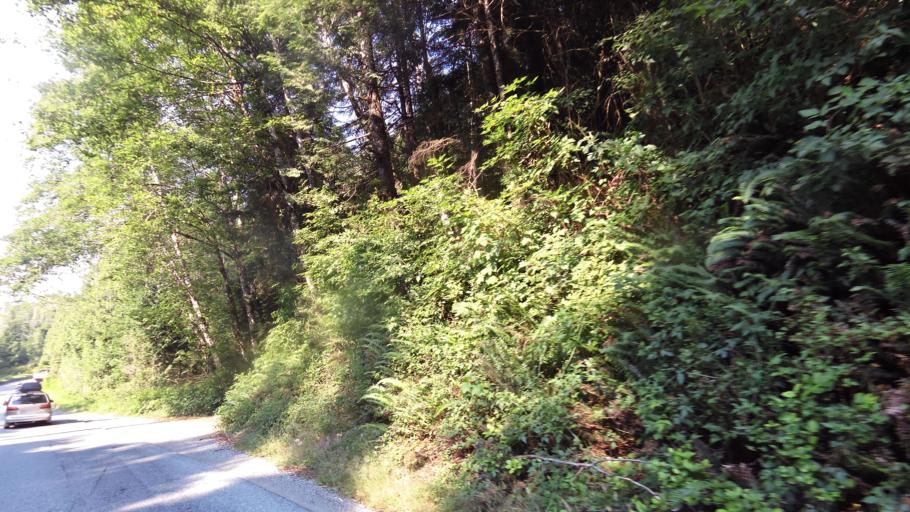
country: CA
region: British Columbia
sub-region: Regional District of Alberni-Clayoquot
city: Ucluelet
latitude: 49.0906
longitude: -125.4528
